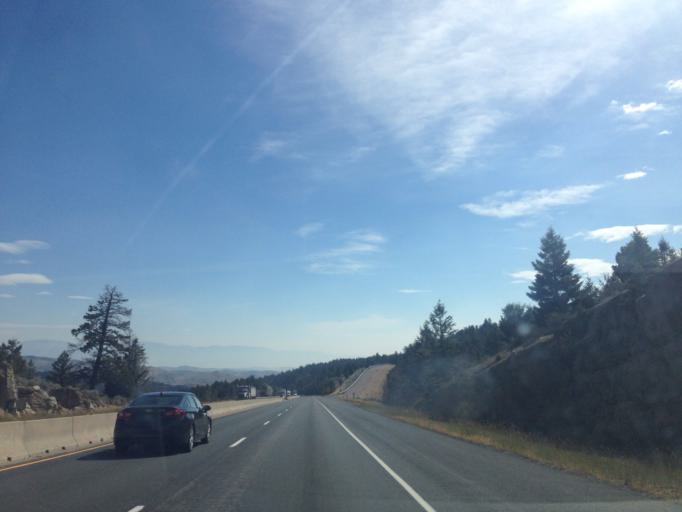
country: US
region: Montana
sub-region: Jefferson County
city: Whitehall
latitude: 45.9100
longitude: -112.3156
